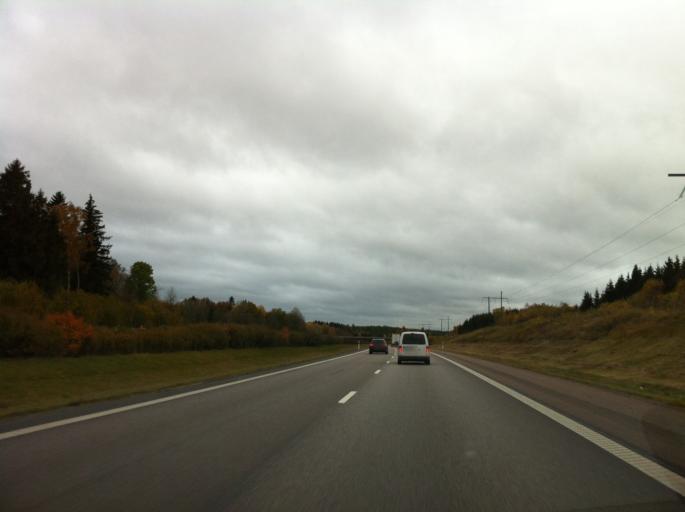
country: SE
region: OEstergoetland
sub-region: Vadstena Kommun
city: Herrestad
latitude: 58.2779
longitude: 14.8664
